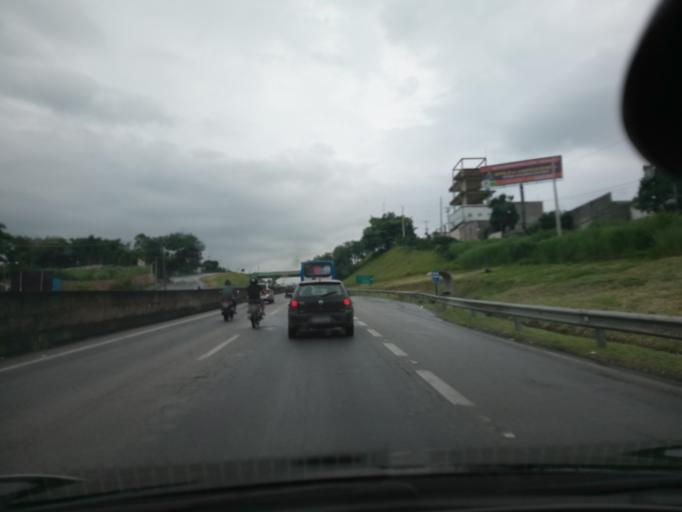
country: BR
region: Sao Paulo
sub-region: Campinas
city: Campinas
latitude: -22.9706
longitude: -47.1018
